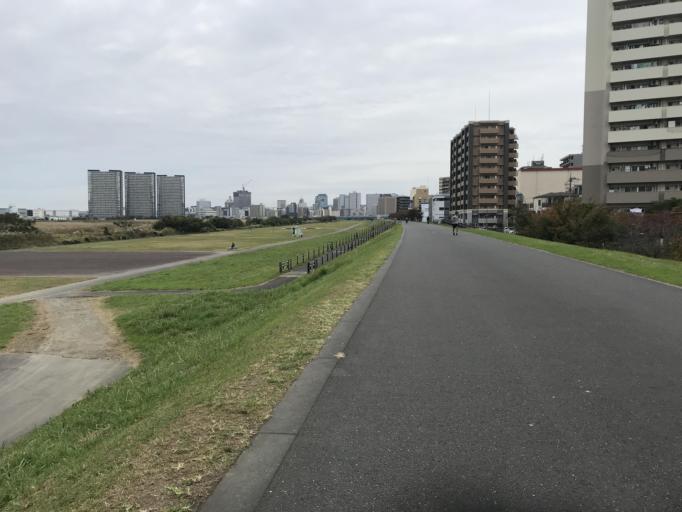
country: JP
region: Kanagawa
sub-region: Kawasaki-shi
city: Kawasaki
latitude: 35.5442
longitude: 139.7218
